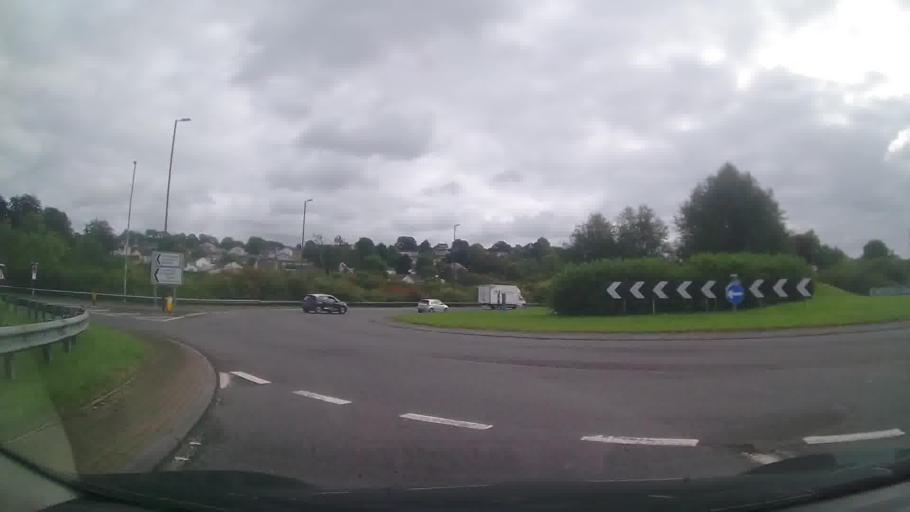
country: GB
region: Wales
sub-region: Carmarthenshire
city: Carmarthen
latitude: 51.8519
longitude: -4.2992
